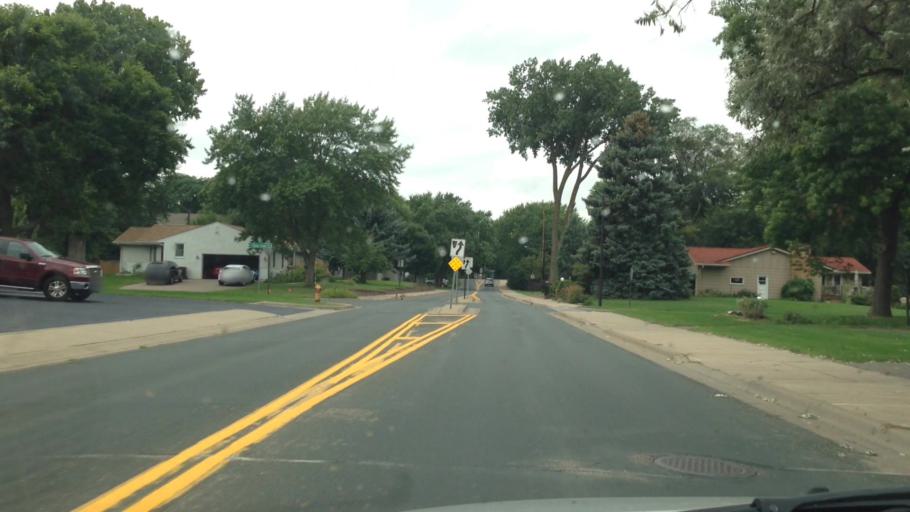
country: US
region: Minnesota
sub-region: Hennepin County
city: Saint Louis Park
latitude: 44.9747
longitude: -93.3774
